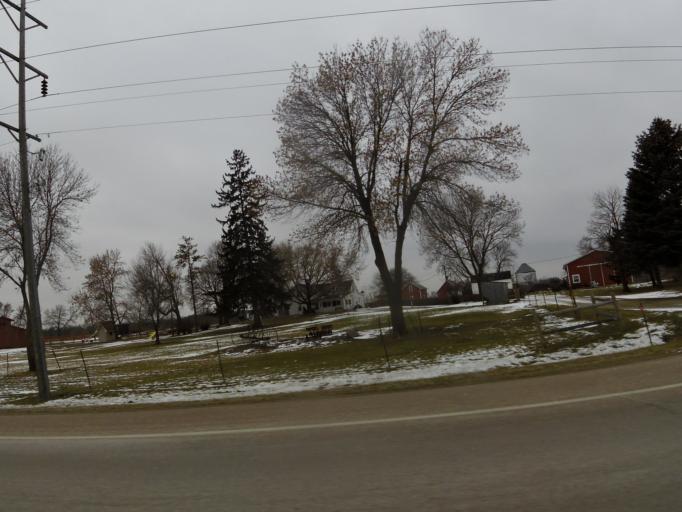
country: US
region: Minnesota
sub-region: Carver County
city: Watertown
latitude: 44.9270
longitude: -93.8308
